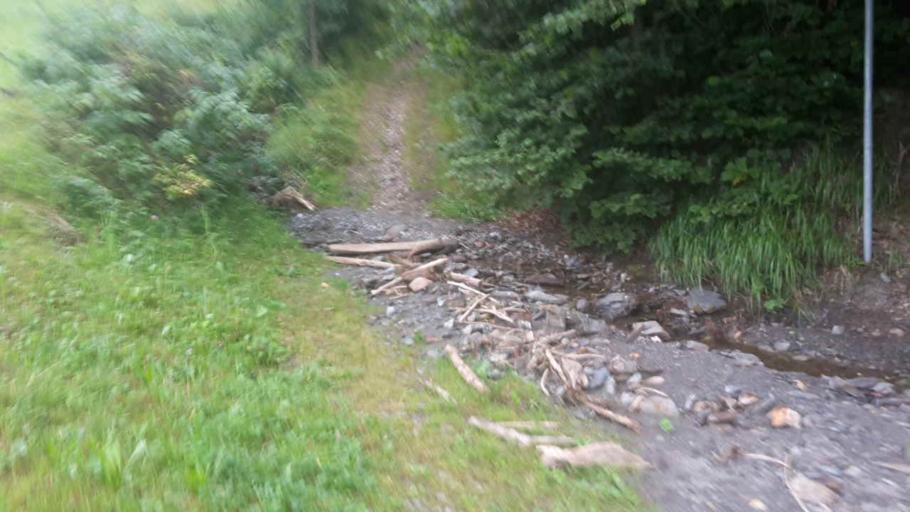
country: AT
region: Tyrol
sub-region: Politischer Bezirk Kitzbuhel
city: Kirchberg in Tirol
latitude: 47.4369
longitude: 12.3265
